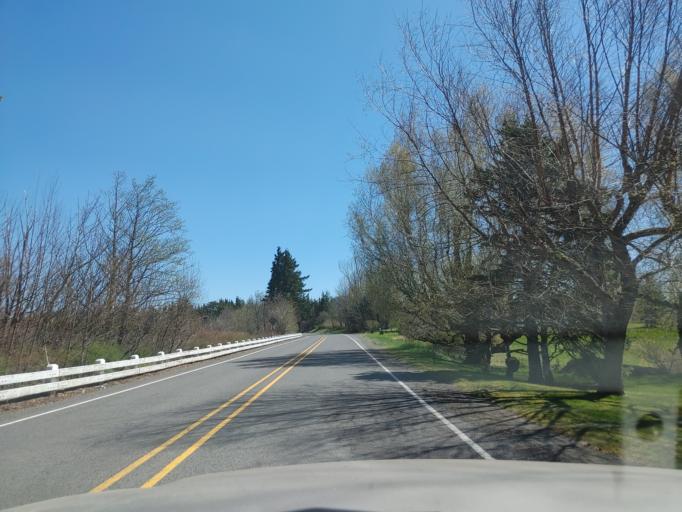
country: US
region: Washington
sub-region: Clark County
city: Washougal
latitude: 45.5329
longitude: -122.2598
